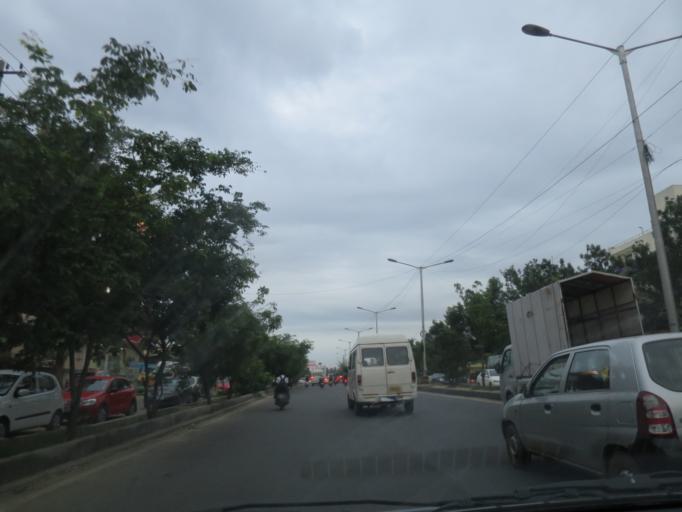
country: IN
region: Karnataka
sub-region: Bangalore Urban
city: Bangalore
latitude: 12.9695
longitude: 77.7009
